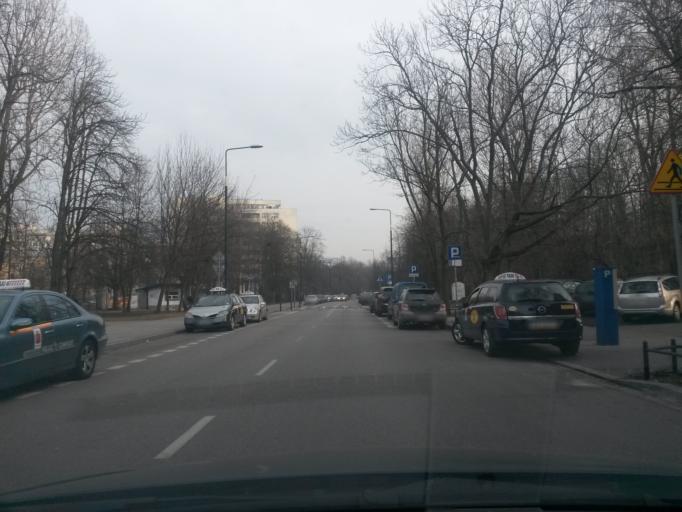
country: PL
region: Masovian Voivodeship
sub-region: Warszawa
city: Srodmiescie
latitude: 52.2298
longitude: 21.0329
